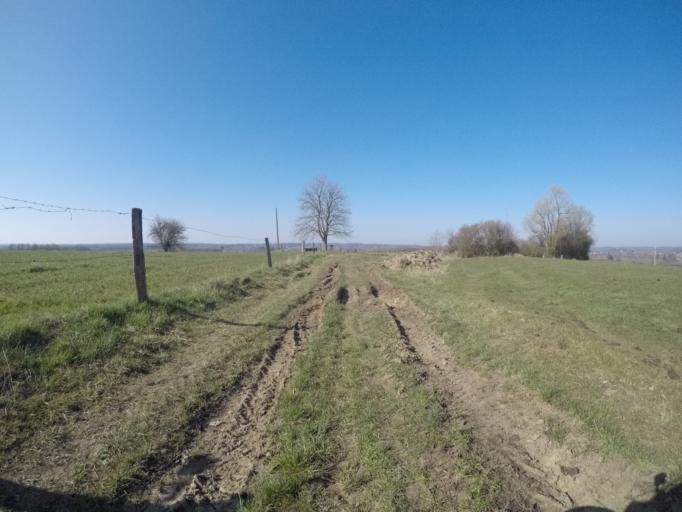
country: BE
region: Wallonia
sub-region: Province du Luxembourg
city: Tintigny
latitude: 49.7063
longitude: 5.5579
